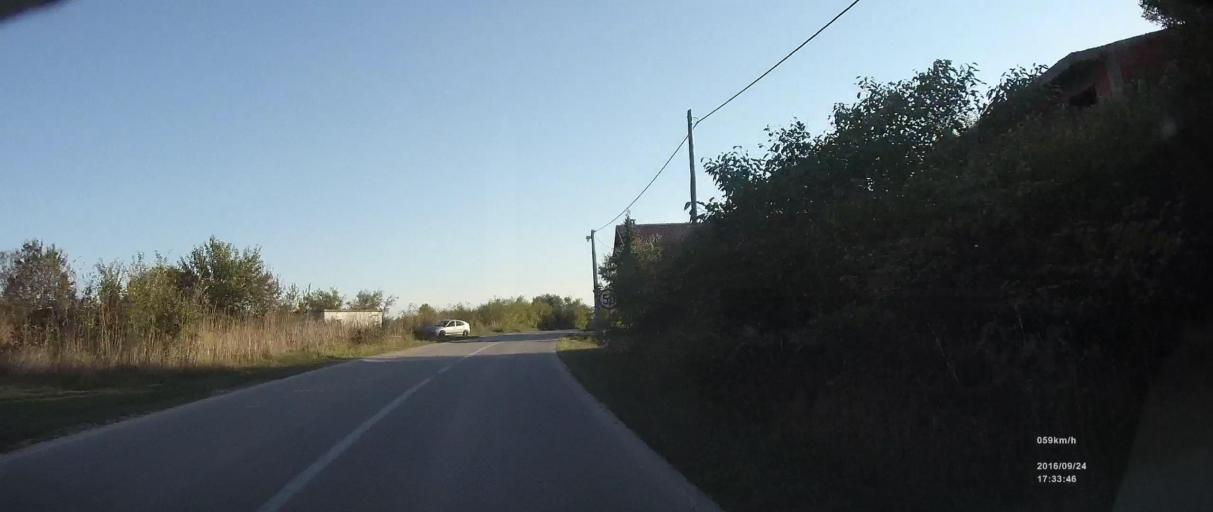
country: HR
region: Zadarska
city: Posedarje
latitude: 44.1714
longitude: 15.4575
